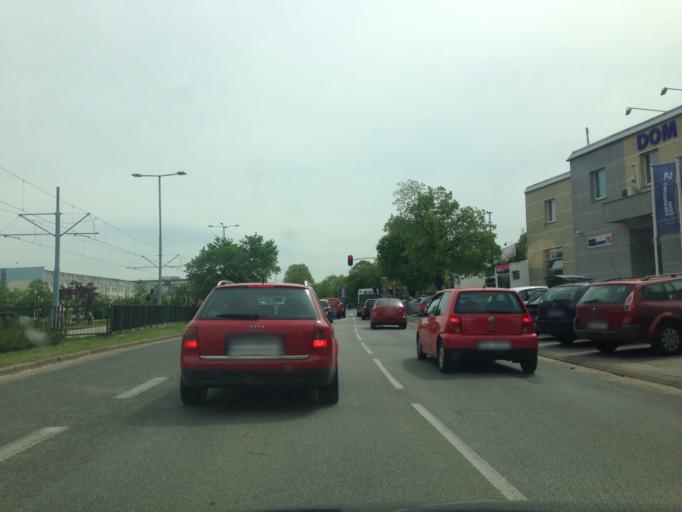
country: PL
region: Pomeranian Voivodeship
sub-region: Sopot
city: Sopot
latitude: 54.4171
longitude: 18.5863
